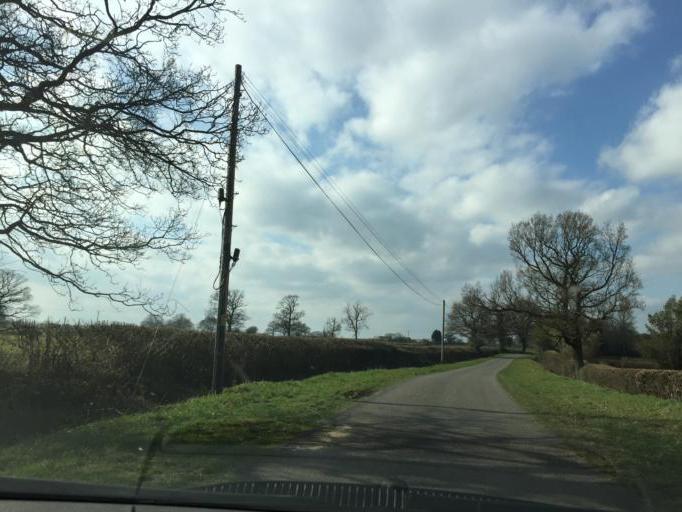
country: GB
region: England
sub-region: Coventry
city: Keresley
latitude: 52.4456
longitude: -1.5812
